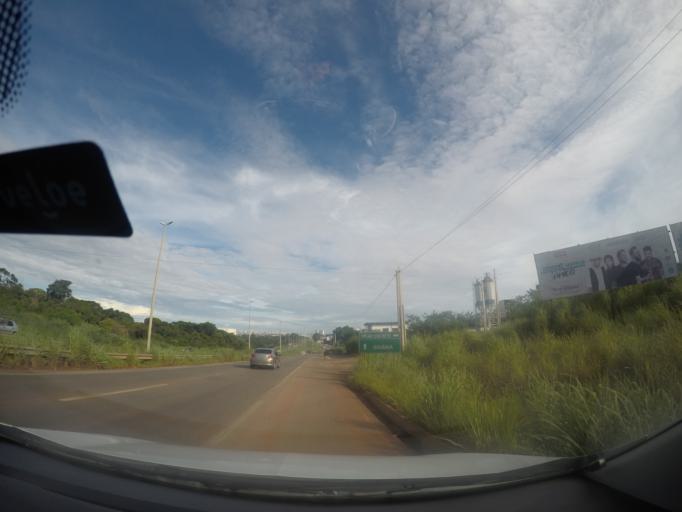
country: BR
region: Goias
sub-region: Goiania
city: Goiania
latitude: -16.6323
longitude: -49.3482
